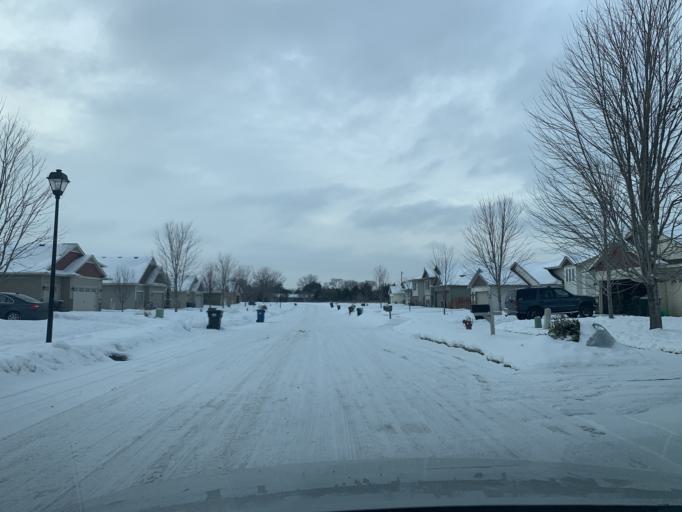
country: US
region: Minnesota
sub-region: Anoka County
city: Ramsey
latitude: 45.2479
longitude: -93.4120
